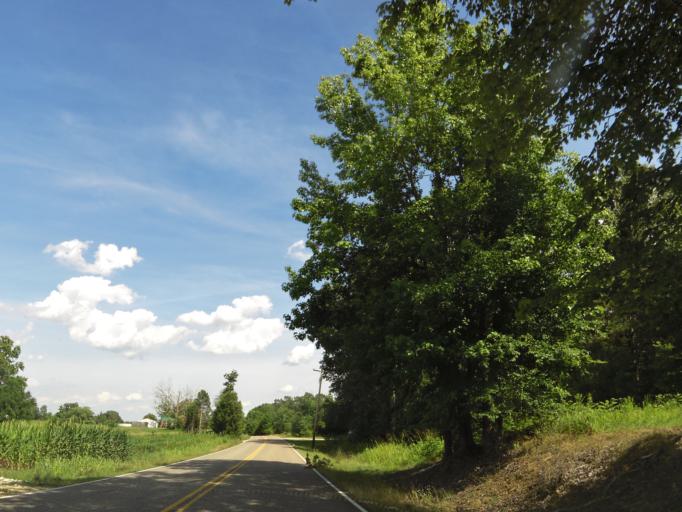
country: US
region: Tennessee
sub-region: Gibson County
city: Milan
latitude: 35.9767
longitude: -88.7218
